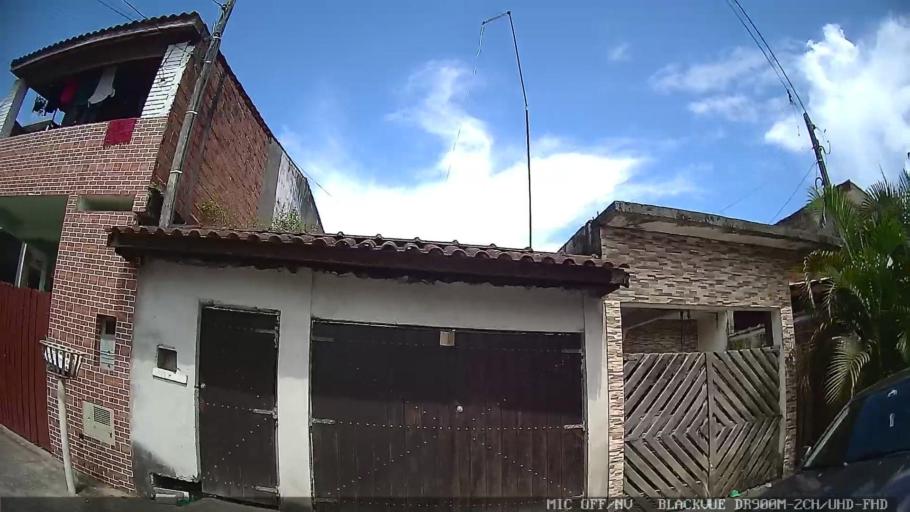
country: BR
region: Sao Paulo
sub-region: Caraguatatuba
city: Caraguatatuba
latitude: -23.6345
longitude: -45.4413
